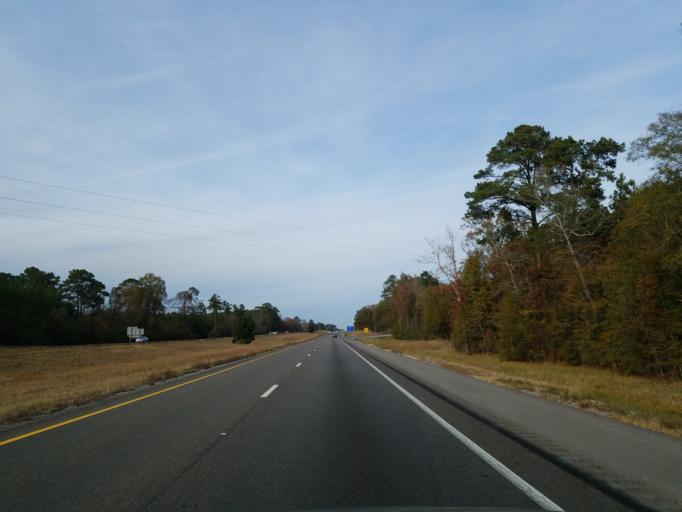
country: US
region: Mississippi
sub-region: Jones County
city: Sharon
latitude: 31.8008
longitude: -89.0538
